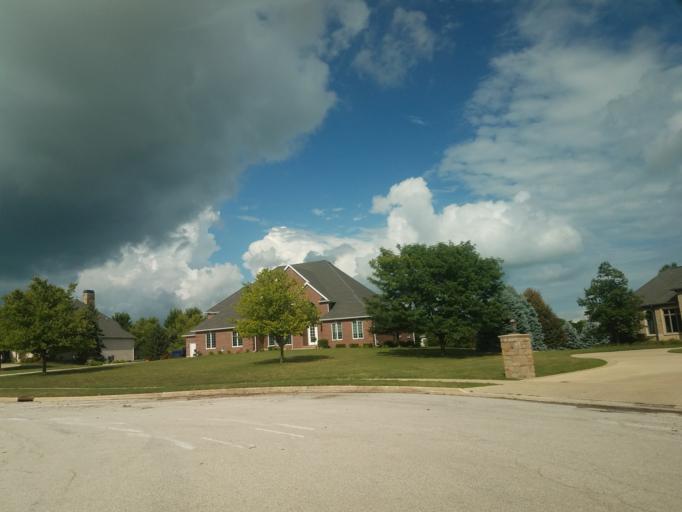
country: US
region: Illinois
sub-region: McLean County
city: Normal
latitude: 40.5077
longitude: -88.9113
